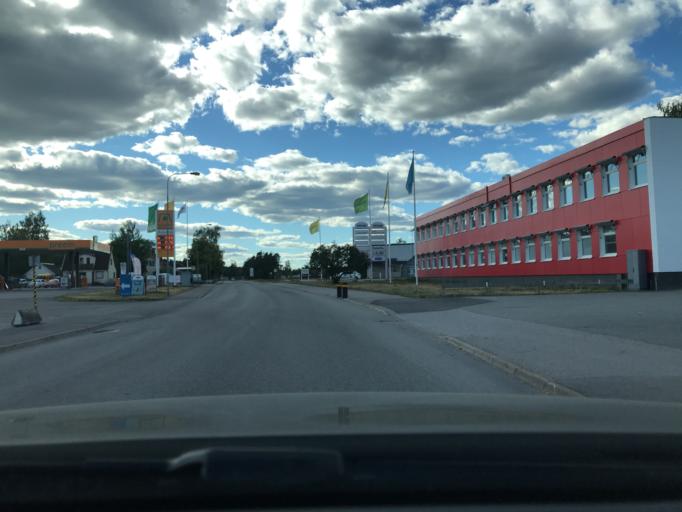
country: SE
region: Kalmar
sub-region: Hultsfreds Kommun
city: Hultsfred
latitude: 57.4940
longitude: 15.8389
